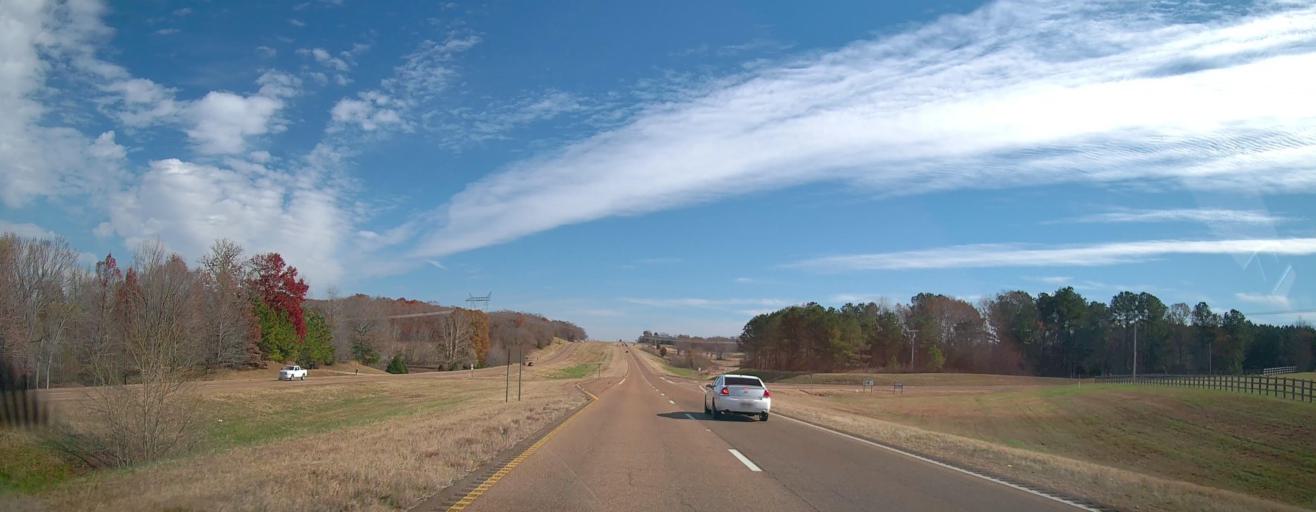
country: US
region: Mississippi
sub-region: Marshall County
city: Holly Springs
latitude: 34.9463
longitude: -89.4051
